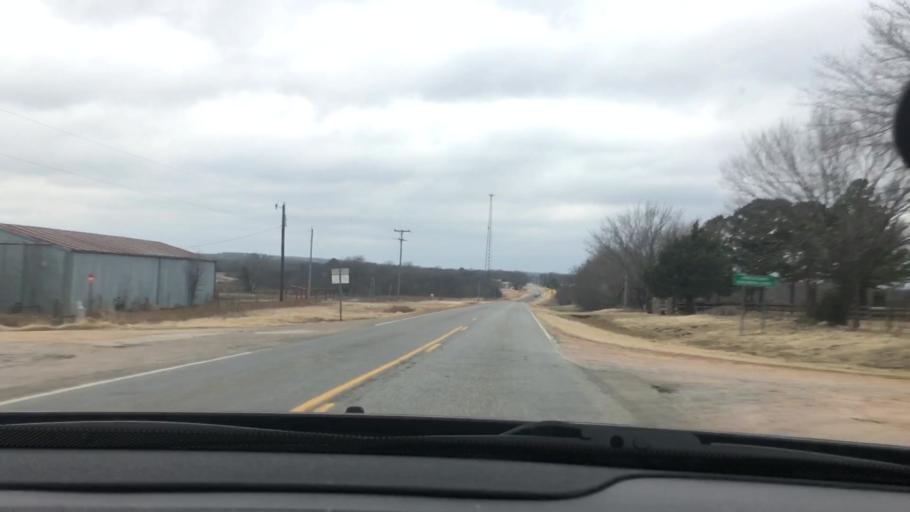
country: US
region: Oklahoma
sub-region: Coal County
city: Coalgate
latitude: 34.3749
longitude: -96.4069
